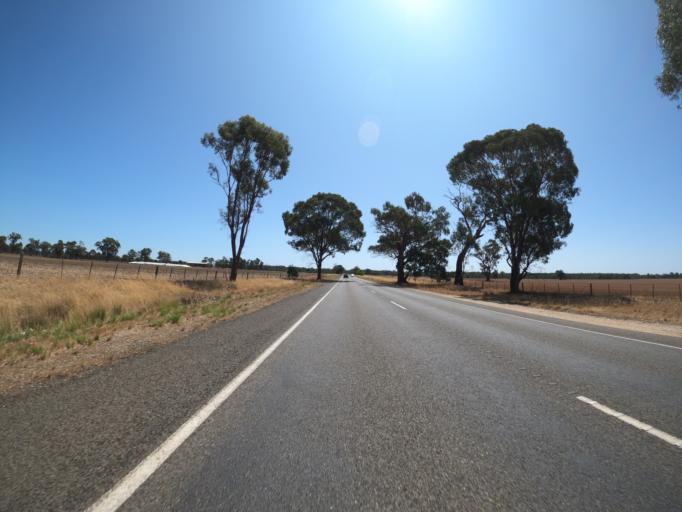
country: AU
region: New South Wales
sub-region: Corowa Shire
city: Corowa
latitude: -36.0713
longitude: 146.2172
